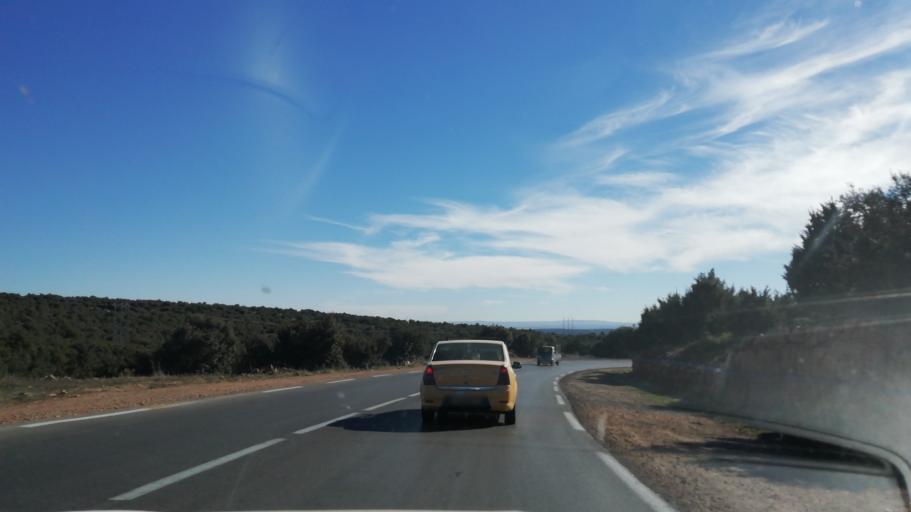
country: DZ
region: Tlemcen
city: Mansoura
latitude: 34.7505
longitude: -1.3440
